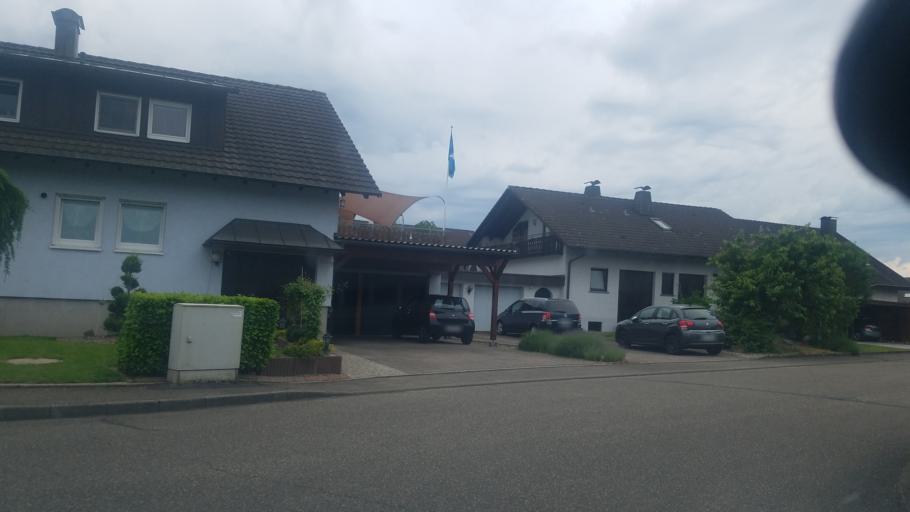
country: DE
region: Baden-Wuerttemberg
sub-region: Freiburg Region
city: Achern
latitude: 48.6503
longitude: 8.0414
